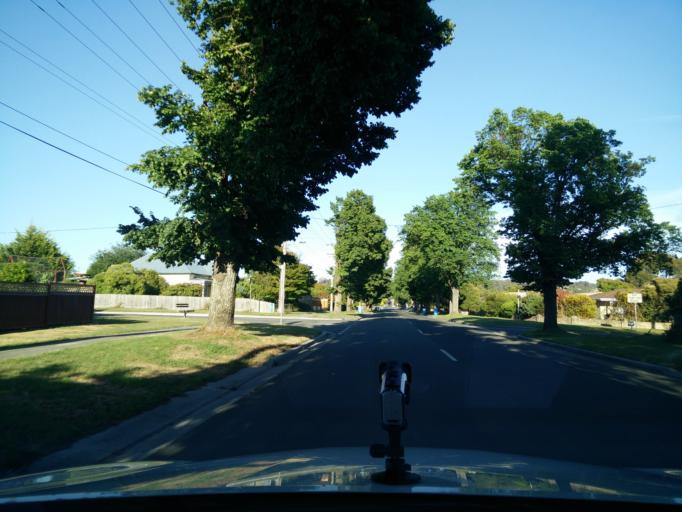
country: AU
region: Tasmania
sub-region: Break O'Day
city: St Helens
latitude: -41.3171
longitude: 148.2418
